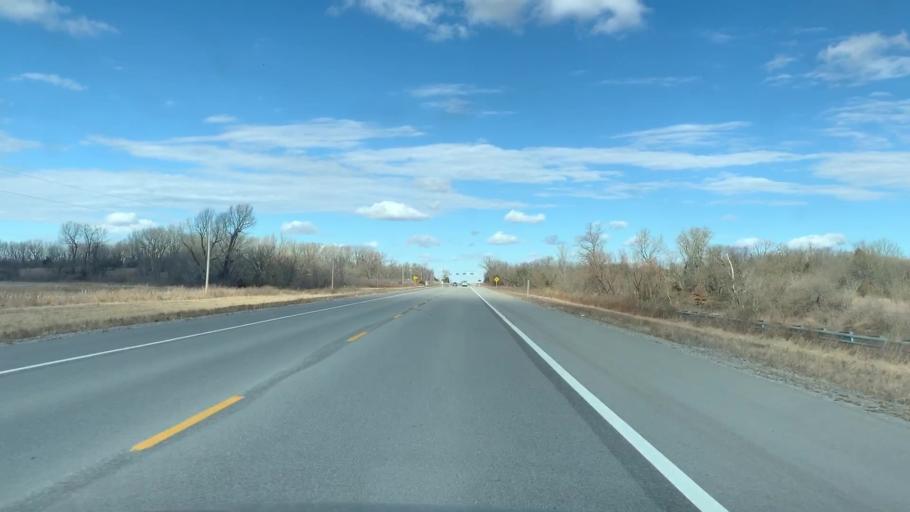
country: US
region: Kansas
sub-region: Cherokee County
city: Columbus
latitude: 37.3176
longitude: -94.8323
